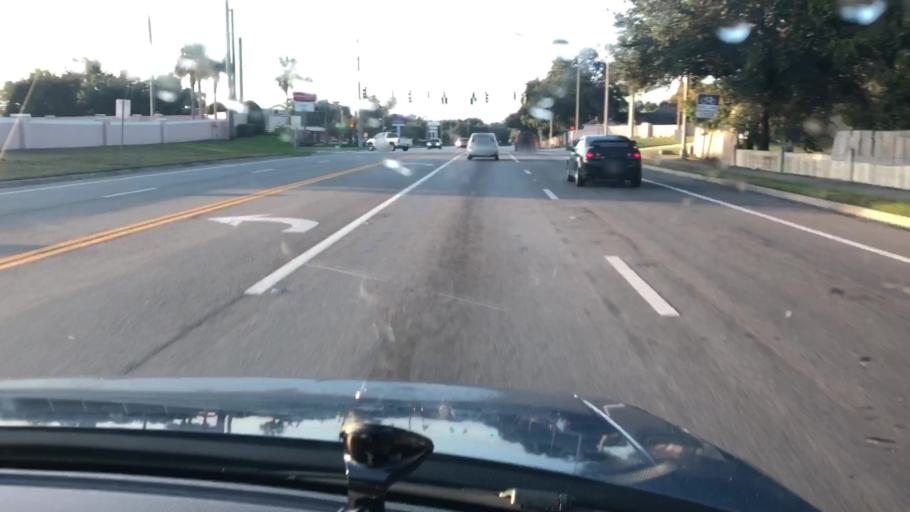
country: US
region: Florida
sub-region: Polk County
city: Gibsonia
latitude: 28.1146
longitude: -81.9466
